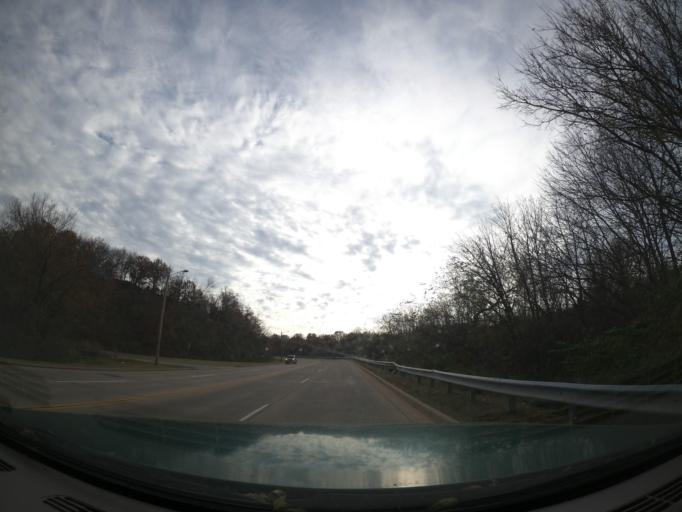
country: US
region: Oklahoma
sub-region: Tulsa County
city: Turley
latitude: 36.2144
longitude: -95.9959
